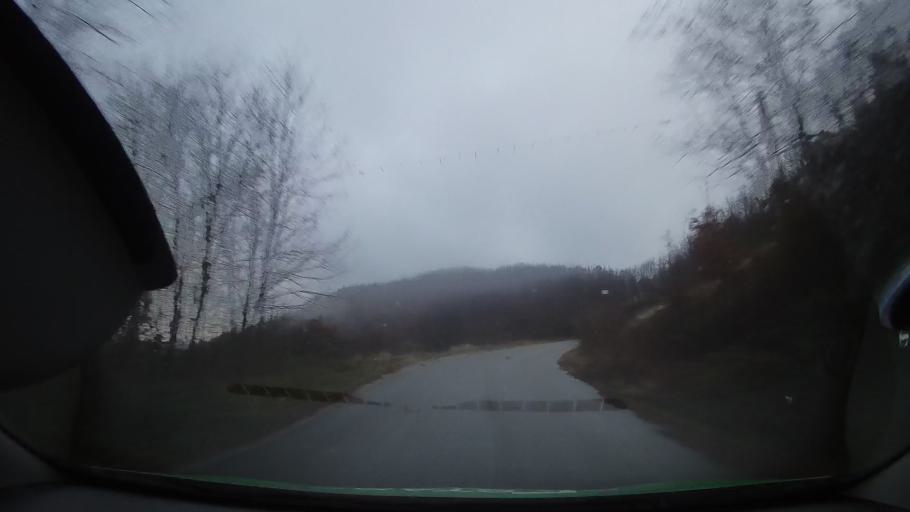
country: RO
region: Hunedoara
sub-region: Comuna Ribita
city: Ribita
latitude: 46.2357
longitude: 22.7465
